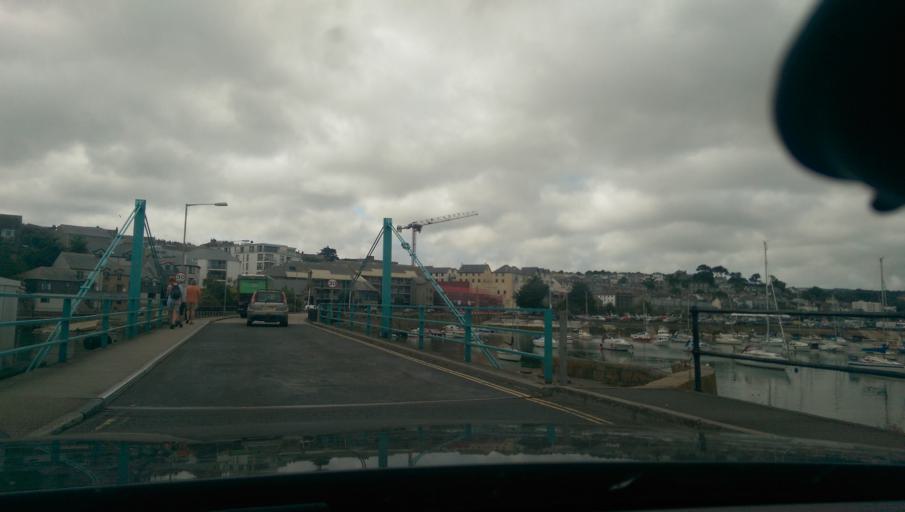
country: GB
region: England
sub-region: Cornwall
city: Penzance
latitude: 50.1175
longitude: -5.5323
